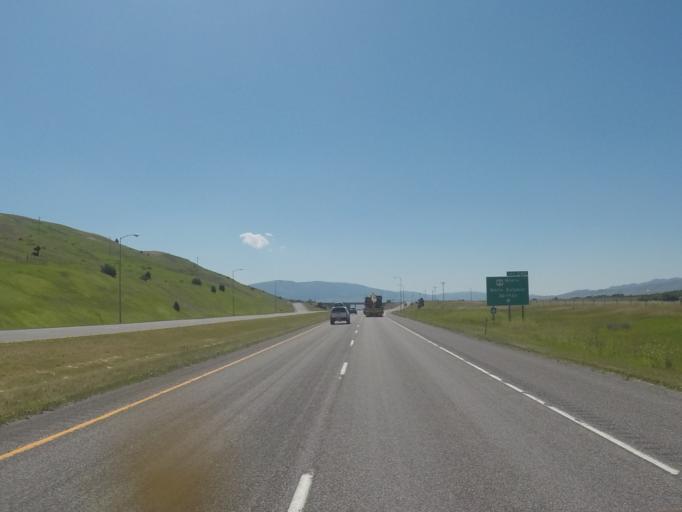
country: US
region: Montana
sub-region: Park County
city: Livingston
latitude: 45.7094
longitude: -110.4487
